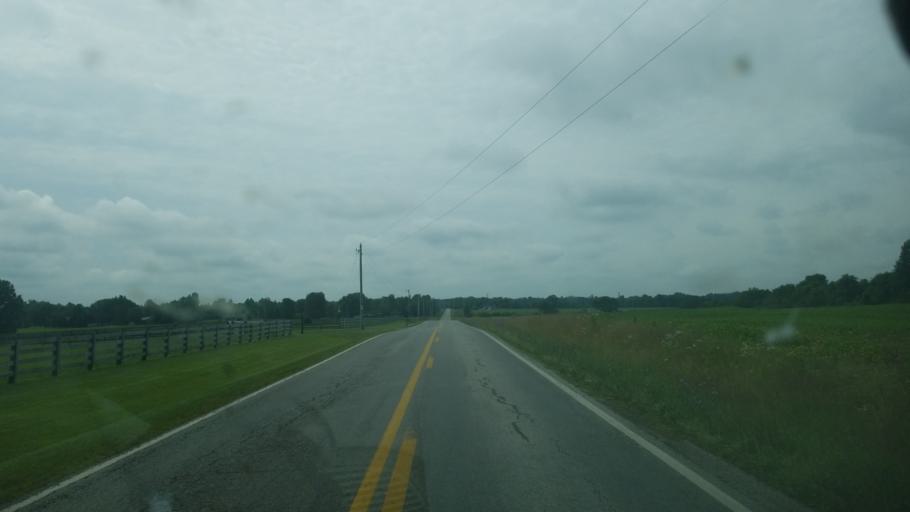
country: US
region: Ohio
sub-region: Franklin County
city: New Albany
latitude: 40.1353
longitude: -82.7612
